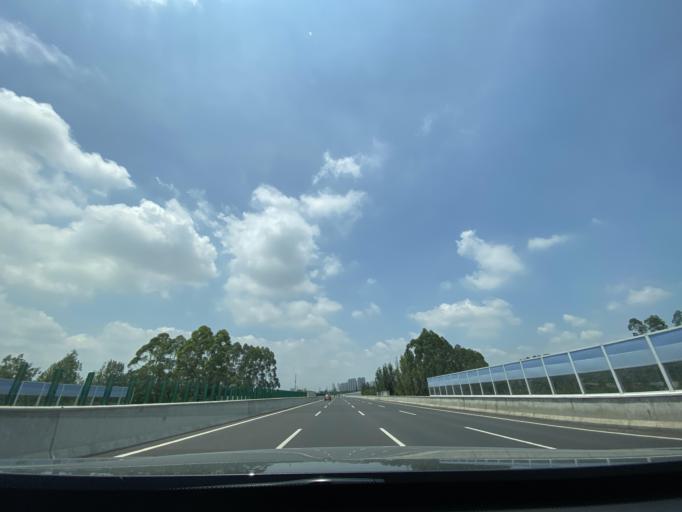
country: CN
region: Sichuan
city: Chengdu
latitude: 30.5785
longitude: 104.1341
